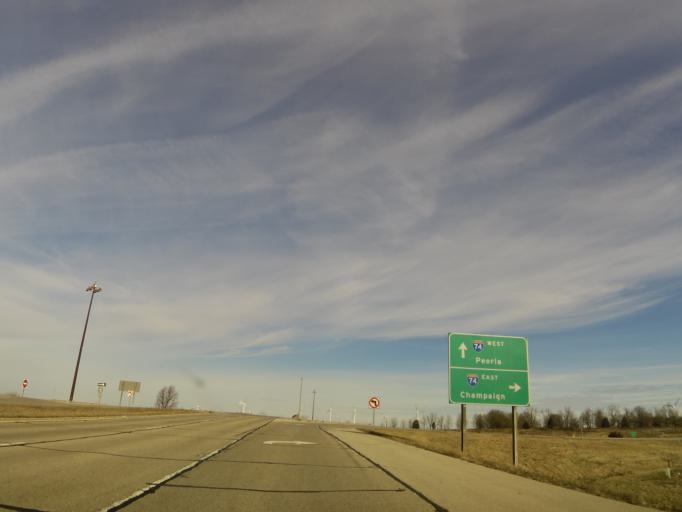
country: US
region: Illinois
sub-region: McLean County
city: Twin Grove
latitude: 40.5384
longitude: -89.0619
